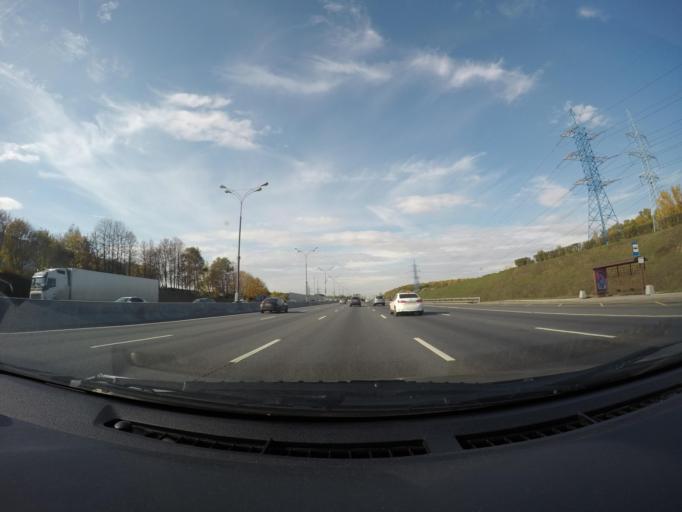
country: RU
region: Moscow
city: Bibirevo
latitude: 55.9028
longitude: 37.6145
